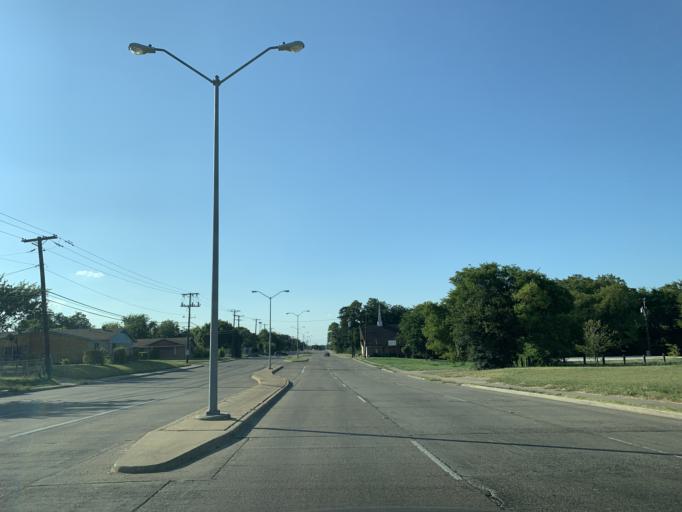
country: US
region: Texas
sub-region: Dallas County
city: Hutchins
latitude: 32.6664
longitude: -96.7586
